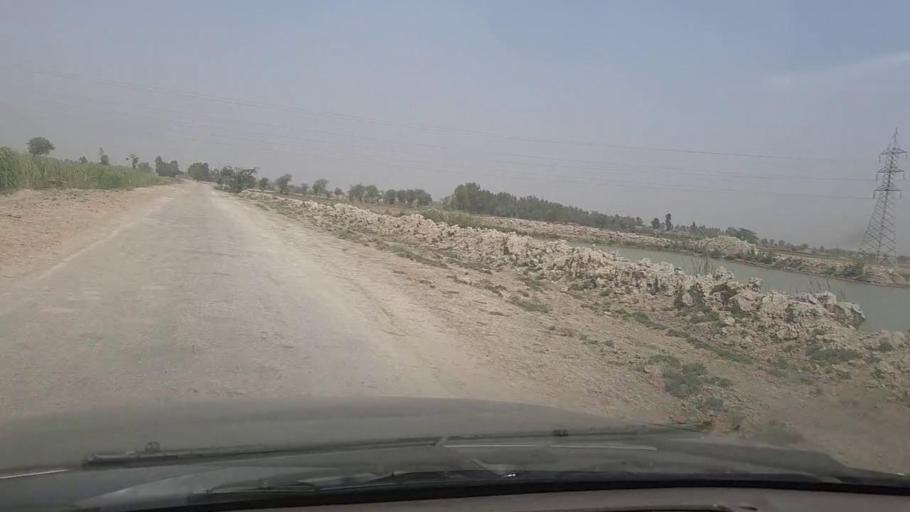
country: PK
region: Sindh
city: Madeji
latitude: 27.8272
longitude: 68.3930
